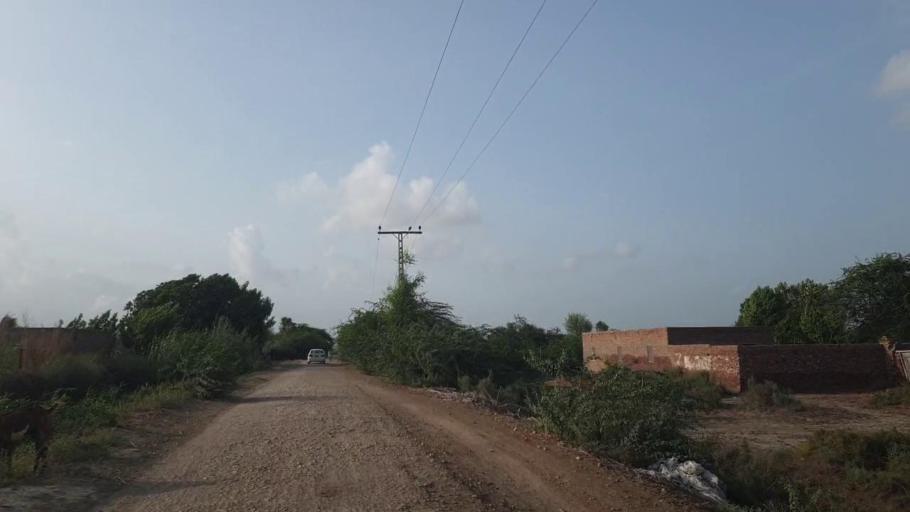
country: PK
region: Sindh
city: Kadhan
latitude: 24.6407
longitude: 69.1117
